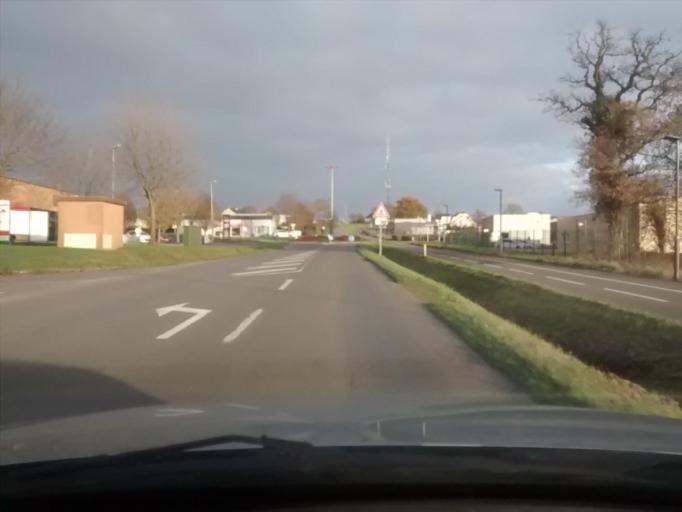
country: FR
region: Pays de la Loire
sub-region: Departement de la Mayenne
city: Change
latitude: 48.1011
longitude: -0.7751
